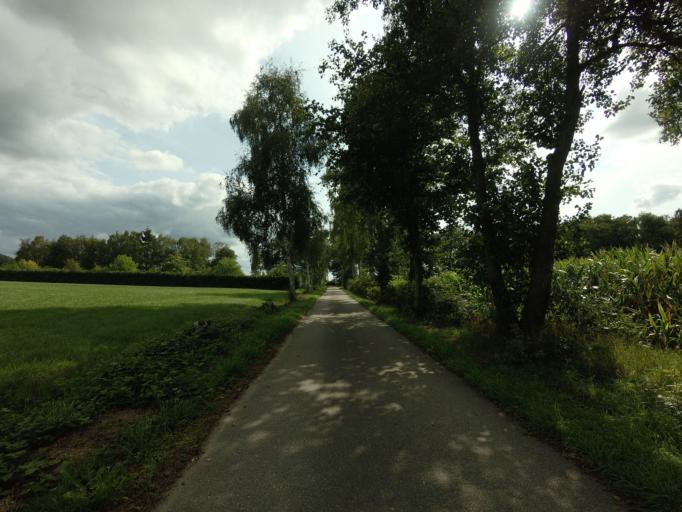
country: NL
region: Overijssel
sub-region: Gemeente Deventer
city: Schalkhaar
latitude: 52.2865
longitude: 6.2506
